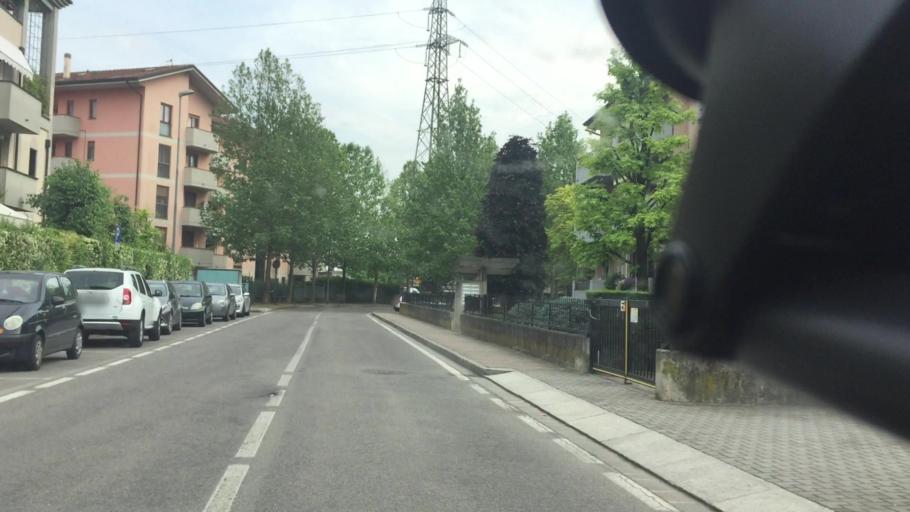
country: IT
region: Lombardy
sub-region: Provincia di Bergamo
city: Treviglio
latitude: 45.5349
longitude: 9.5966
